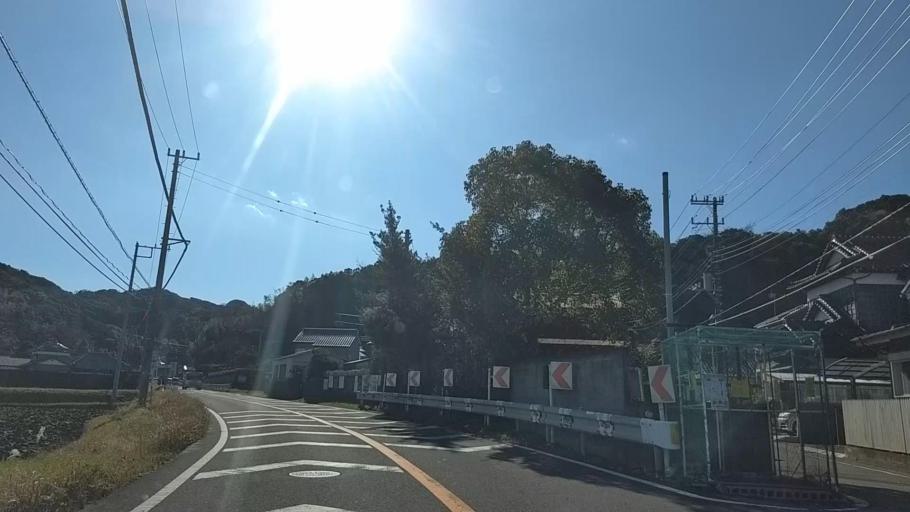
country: JP
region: Chiba
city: Tateyama
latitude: 34.9751
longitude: 139.8632
